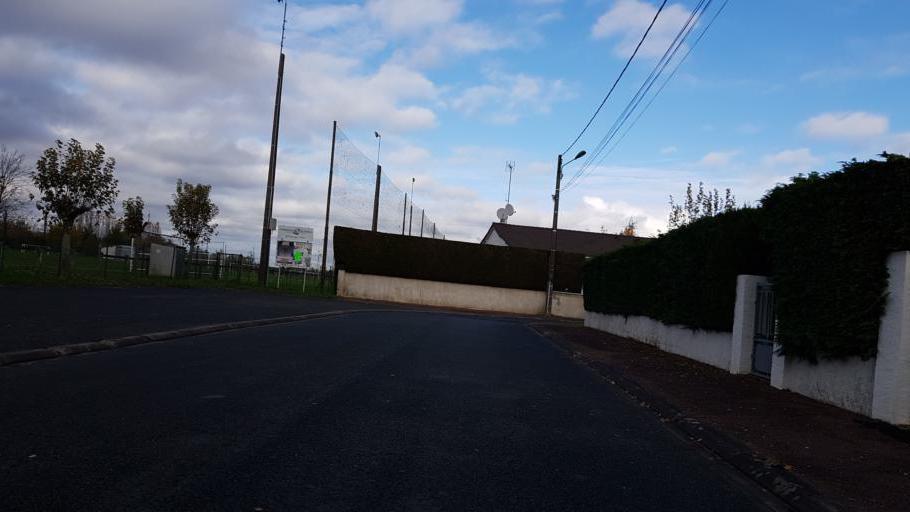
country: FR
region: Poitou-Charentes
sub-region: Departement de la Vienne
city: Chasseneuil-du-Poitou
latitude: 46.6576
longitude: 0.3784
